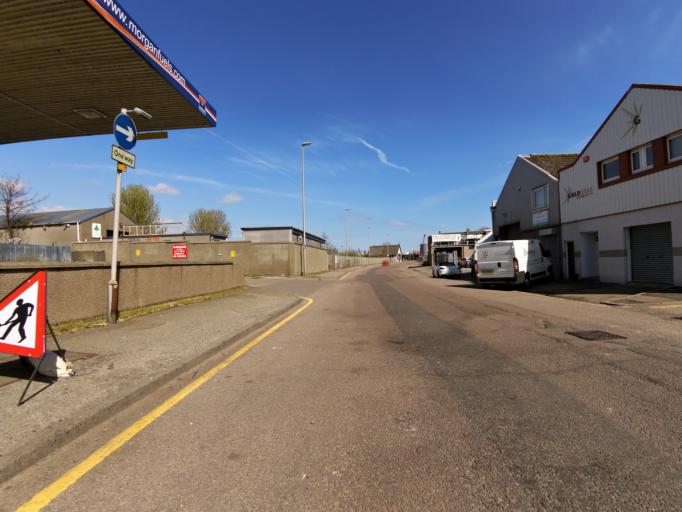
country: GB
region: Scotland
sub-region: Aberdeen City
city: Aberdeen
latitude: 57.1382
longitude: -2.0917
